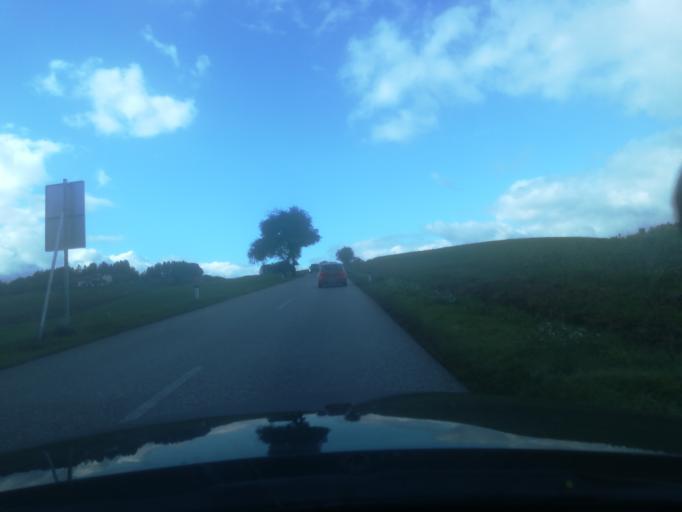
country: AT
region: Upper Austria
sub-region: Linz Stadt
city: Linz
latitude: 48.3478
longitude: 14.2699
